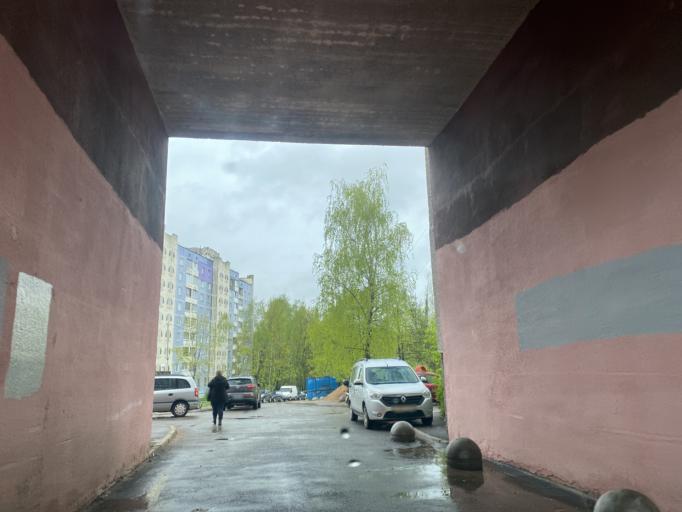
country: BY
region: Minsk
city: Bal'shavik
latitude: 53.9585
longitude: 27.6125
